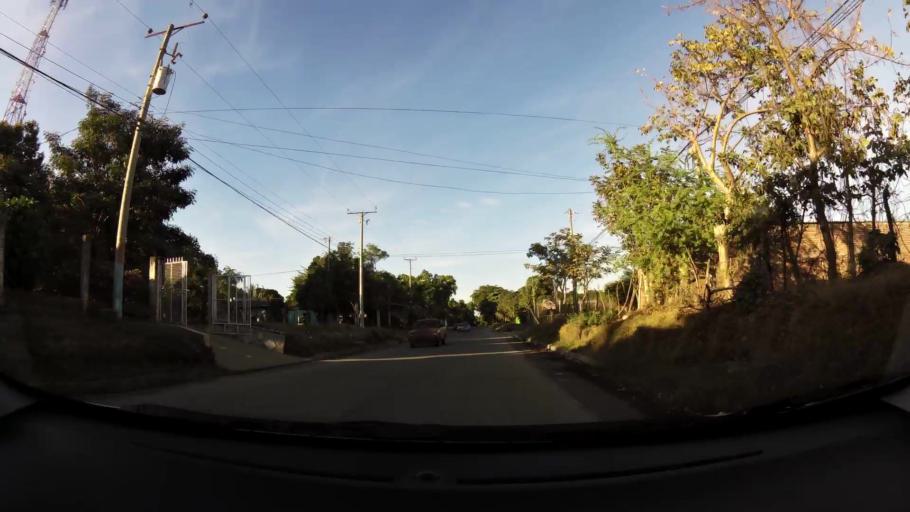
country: SV
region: San Miguel
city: San Miguel
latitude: 13.4574
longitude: -88.1769
